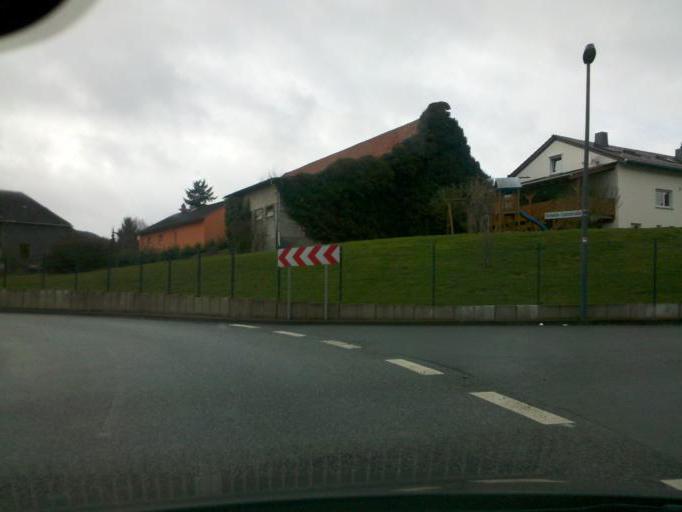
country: DE
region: Hesse
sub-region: Regierungsbezirk Giessen
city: Breidenbach
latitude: 50.8462
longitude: 8.5082
